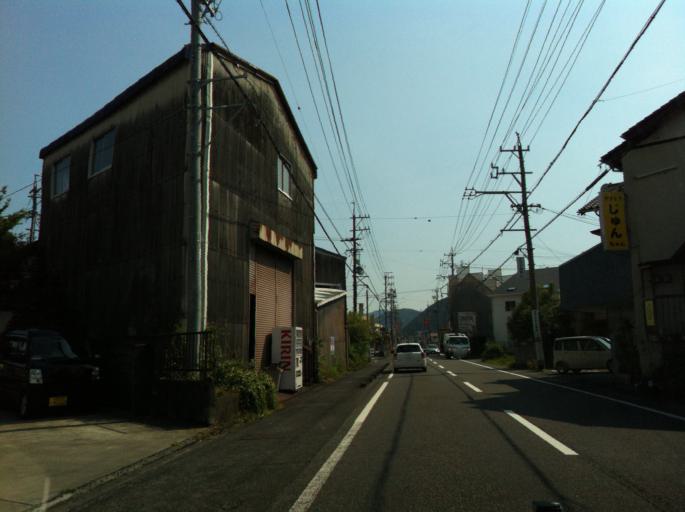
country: JP
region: Shizuoka
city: Shizuoka-shi
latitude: 35.0207
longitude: 138.3604
